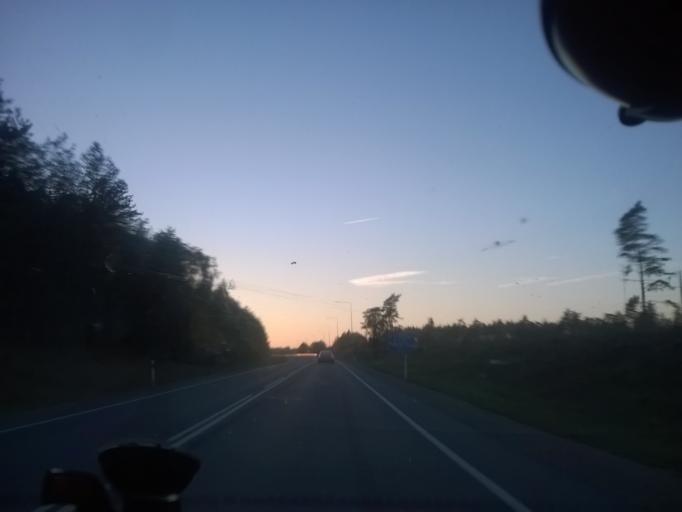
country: EE
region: Laeaene
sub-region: Lihula vald
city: Lihula
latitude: 58.9734
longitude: 23.9078
